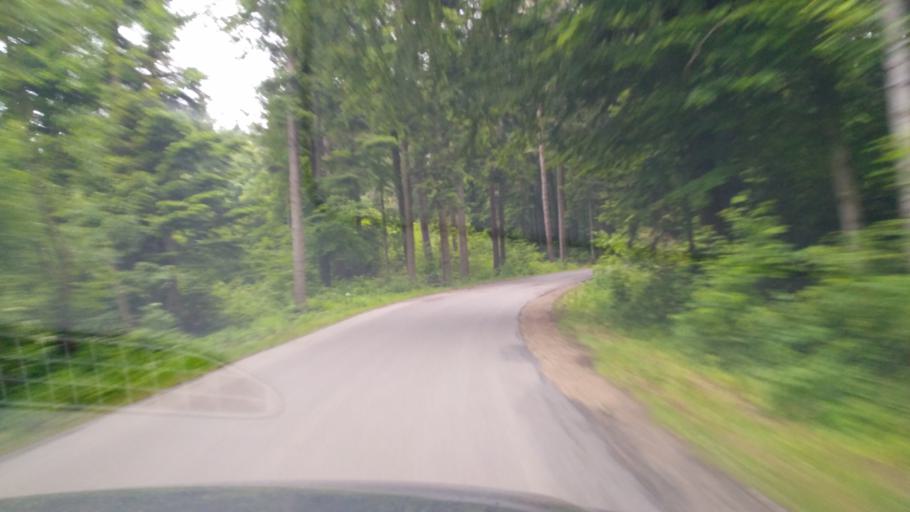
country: PL
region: Subcarpathian Voivodeship
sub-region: Powiat brzozowski
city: Orzechowka
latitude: 49.7246
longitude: 21.9156
